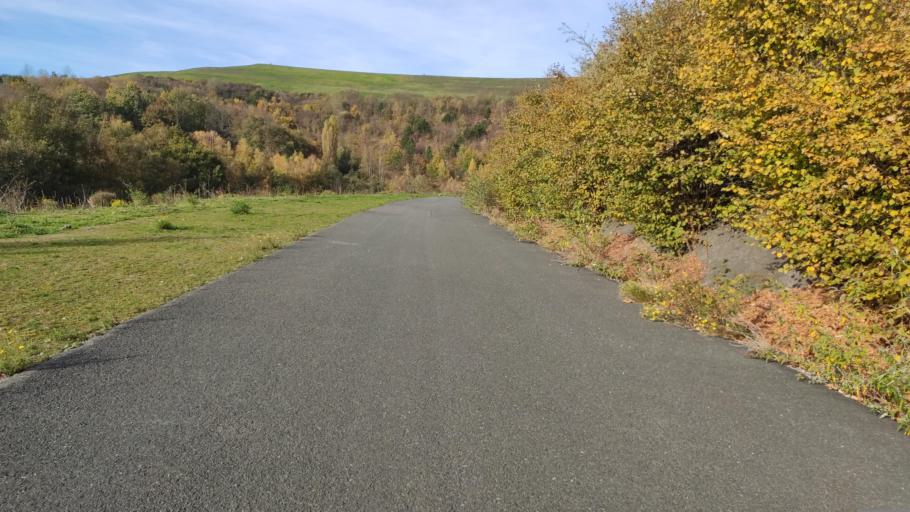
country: DE
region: North Rhine-Westphalia
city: Herten
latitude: 51.5641
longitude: 7.1670
